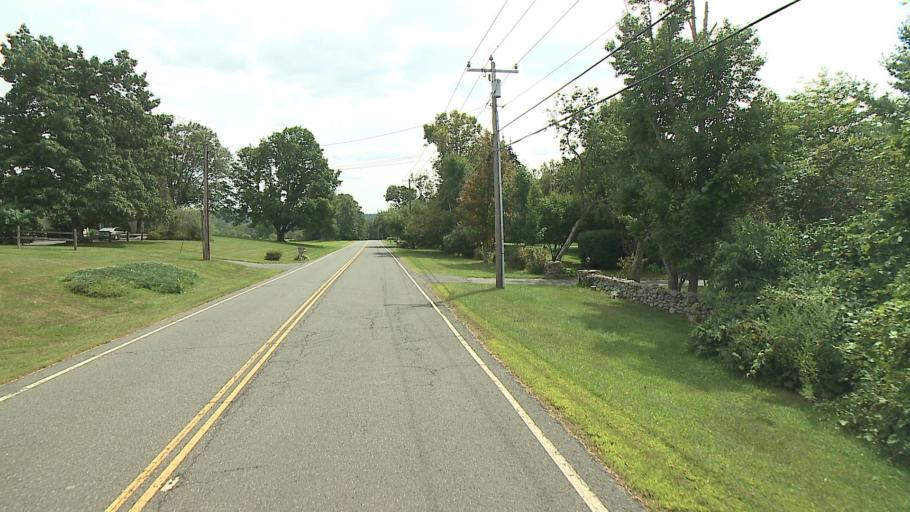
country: US
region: Connecticut
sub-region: Litchfield County
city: Bethlehem Village
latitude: 41.5981
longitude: -73.2388
